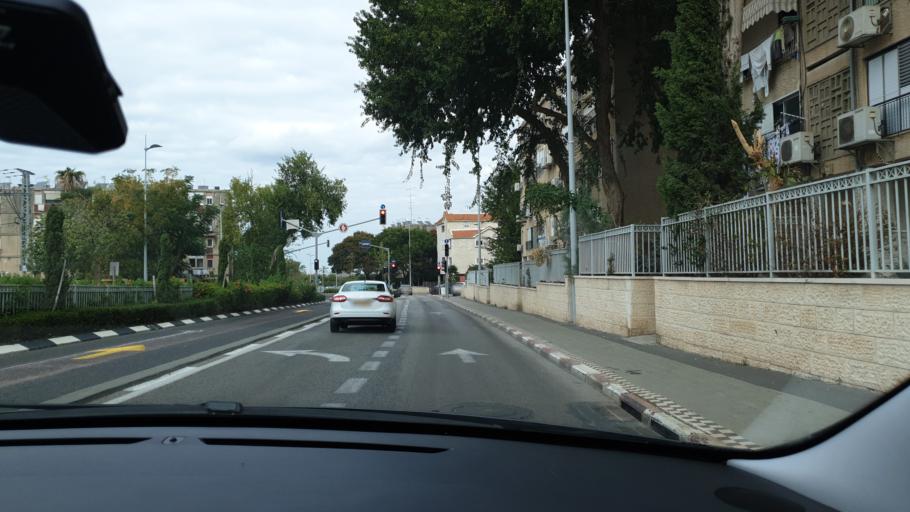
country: IL
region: Haifa
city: Qiryat Ata
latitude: 32.8159
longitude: 35.1135
